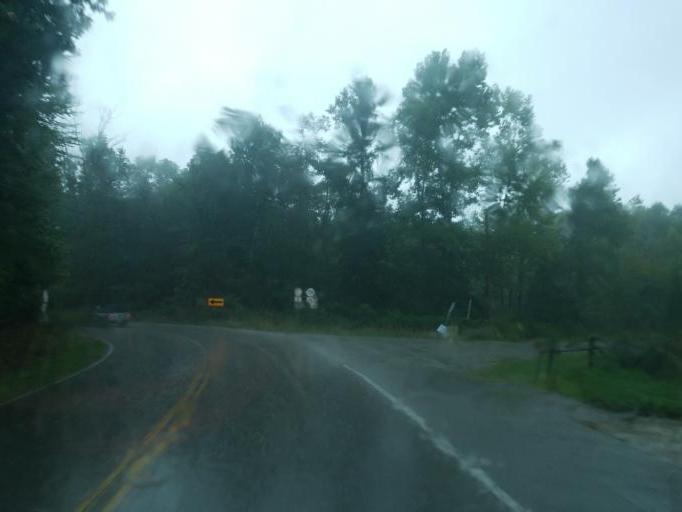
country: US
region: Kentucky
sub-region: Carter County
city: Olive Hill
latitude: 38.3446
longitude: -83.2003
